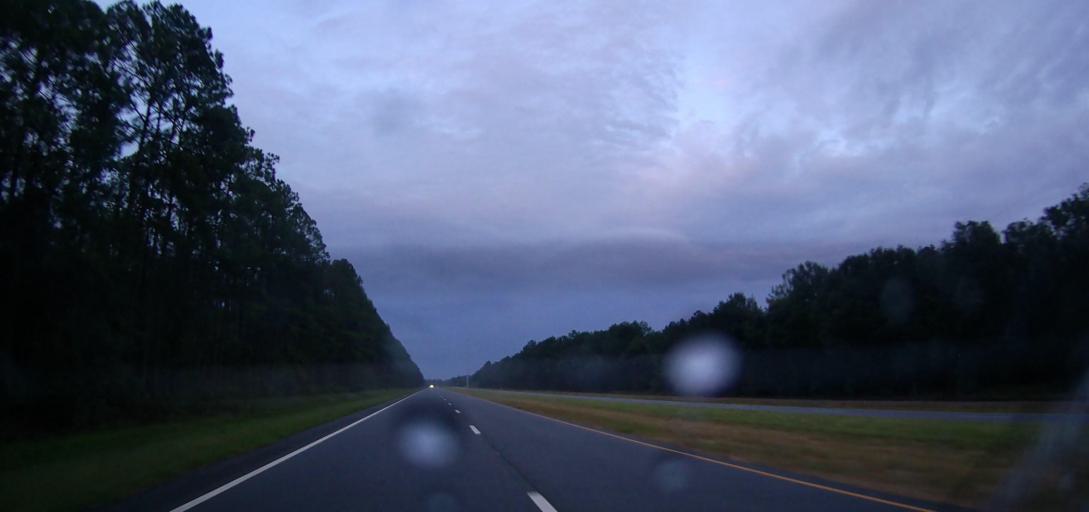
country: US
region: Georgia
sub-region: Lanier County
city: Lakeland
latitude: 30.8952
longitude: -83.1121
